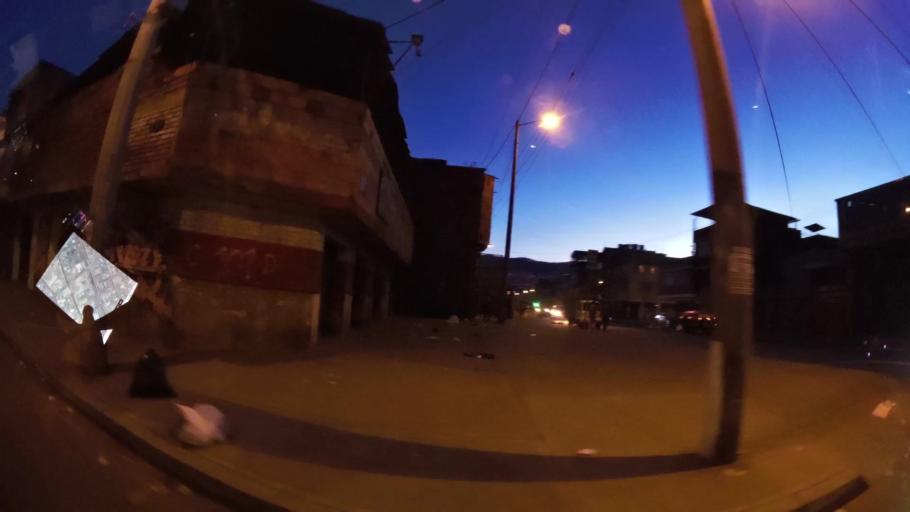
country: CO
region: Bogota D.C.
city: Bogota
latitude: 4.5621
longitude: -74.1303
